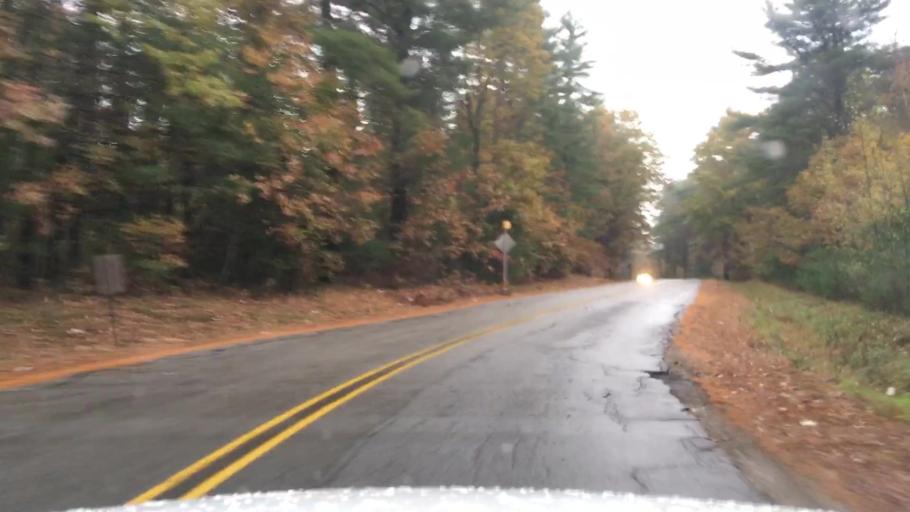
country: US
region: Maine
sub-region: York County
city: Berwick
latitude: 43.2801
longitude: -70.9059
